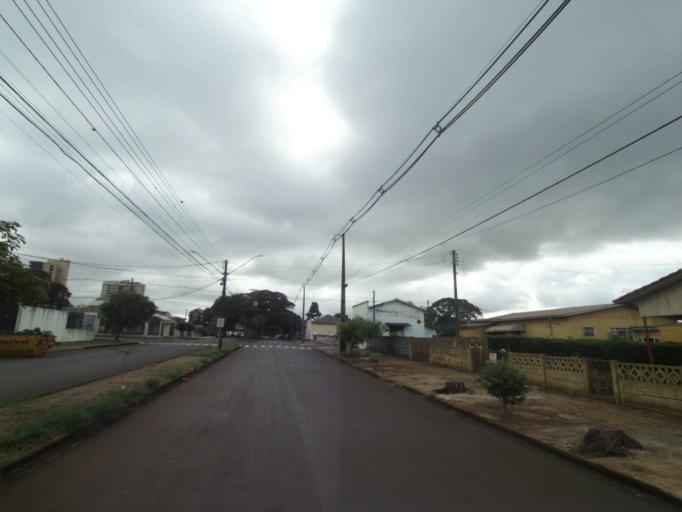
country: BR
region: Parana
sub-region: Campo Mourao
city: Campo Mourao
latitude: -24.0477
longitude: -52.3751
